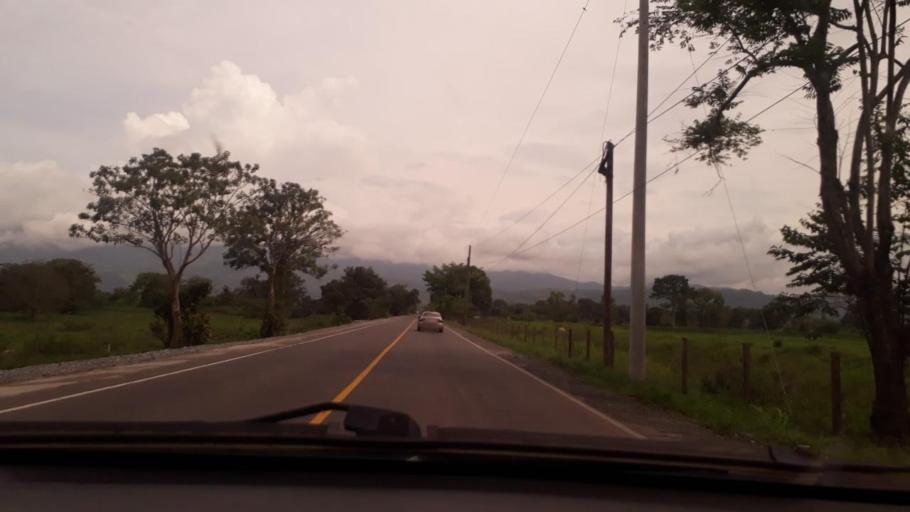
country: HN
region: Cortes
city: Potrerillos
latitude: 15.6235
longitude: -88.4006
